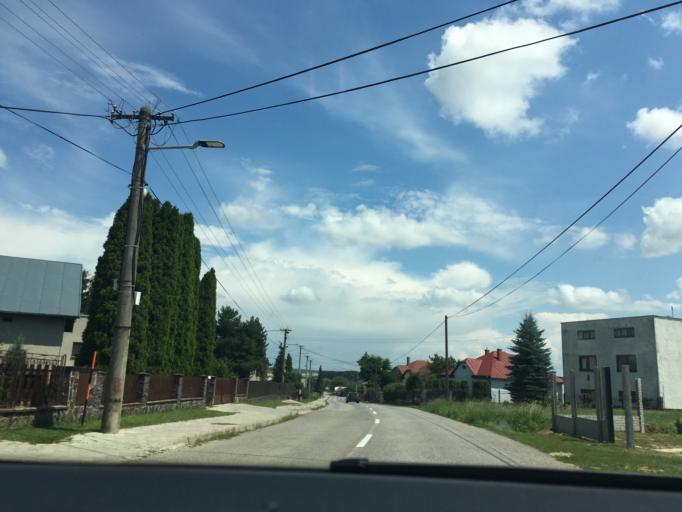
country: SK
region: Presovsky
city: Vranov nad Topl'ou
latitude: 48.8237
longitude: 21.6967
